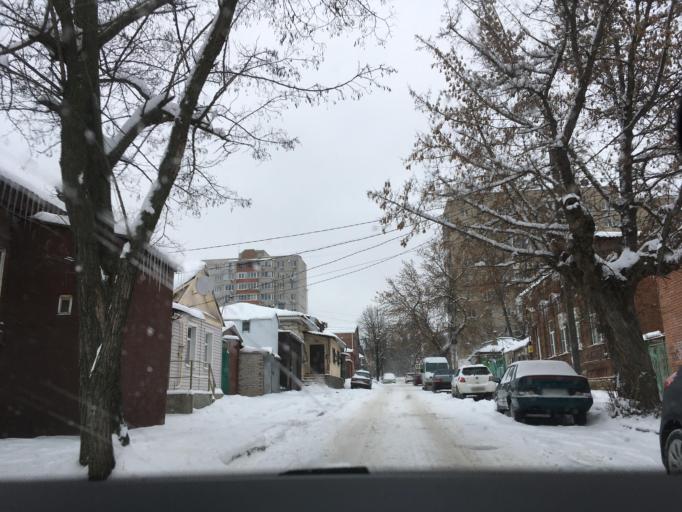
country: RU
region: Rostov
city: Rostov-na-Donu
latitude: 47.2262
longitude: 39.7558
